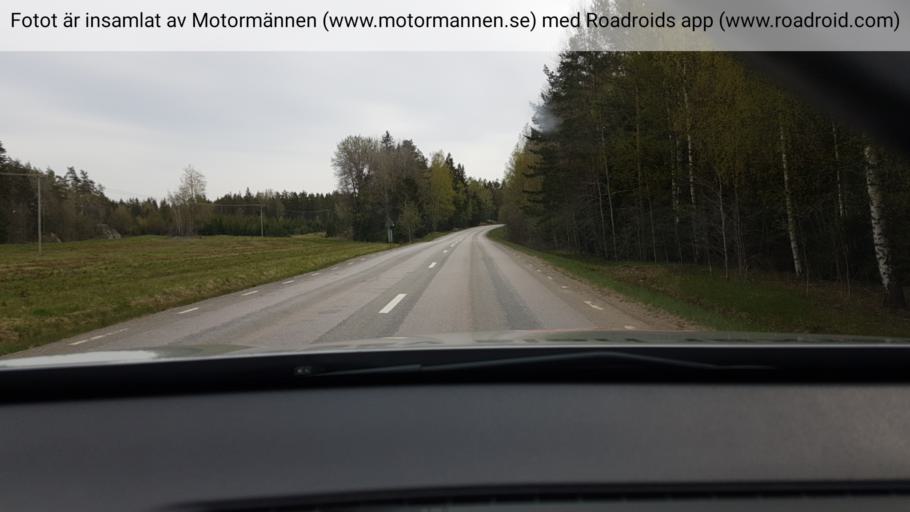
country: SE
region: Stockholm
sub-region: Norrtalje Kommun
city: Nykvarn
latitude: 59.9062
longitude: 18.0963
